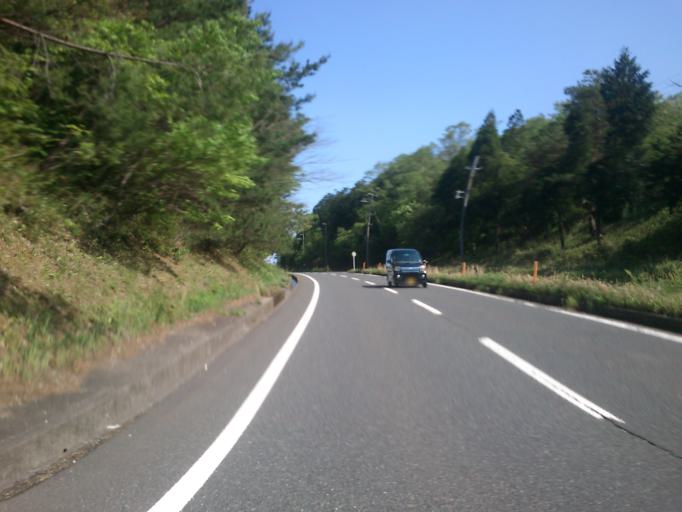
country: JP
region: Kyoto
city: Miyazu
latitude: 35.6622
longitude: 135.1035
